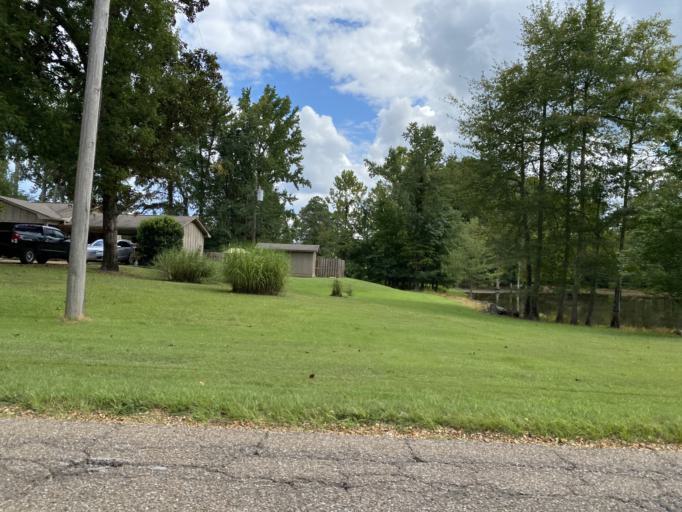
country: US
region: Mississippi
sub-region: Monroe County
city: Amory
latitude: 33.9715
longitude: -88.4511
